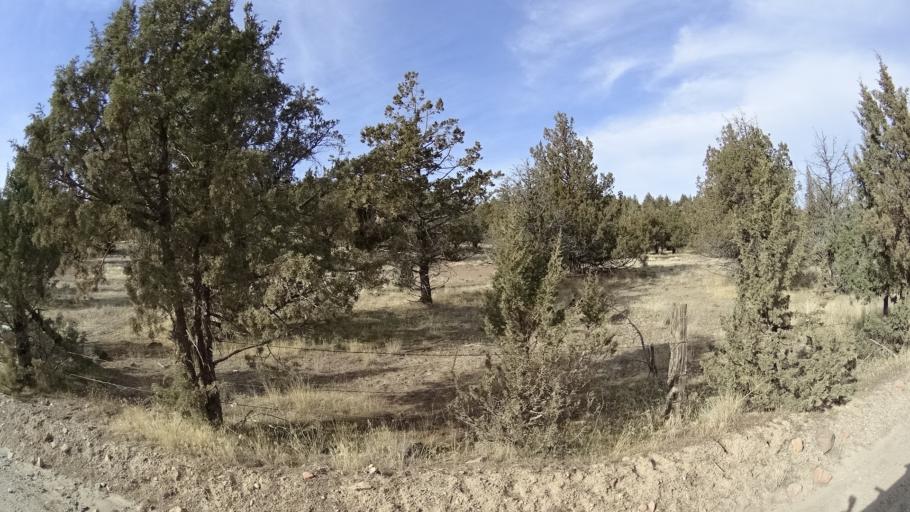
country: US
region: California
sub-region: Siskiyou County
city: Montague
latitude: 41.5897
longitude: -122.4403
